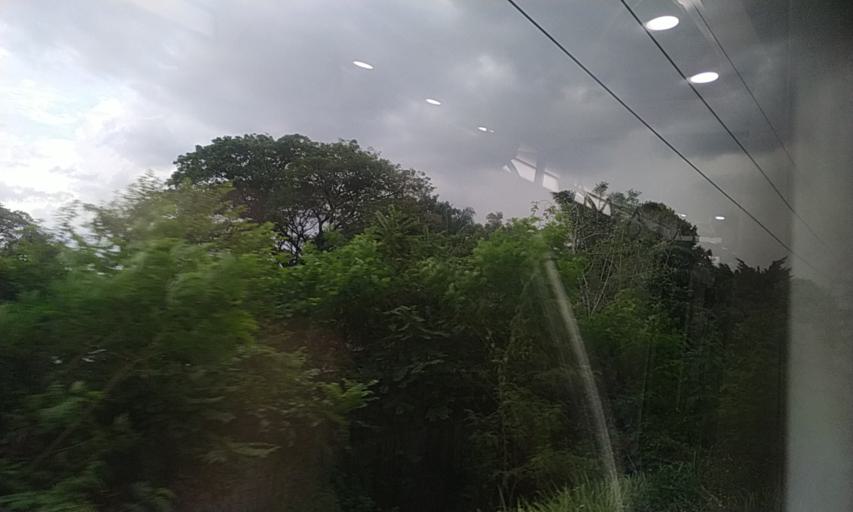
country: MY
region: Kuala Lumpur
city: Kuala Lumpur
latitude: 3.2311
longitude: 101.6752
